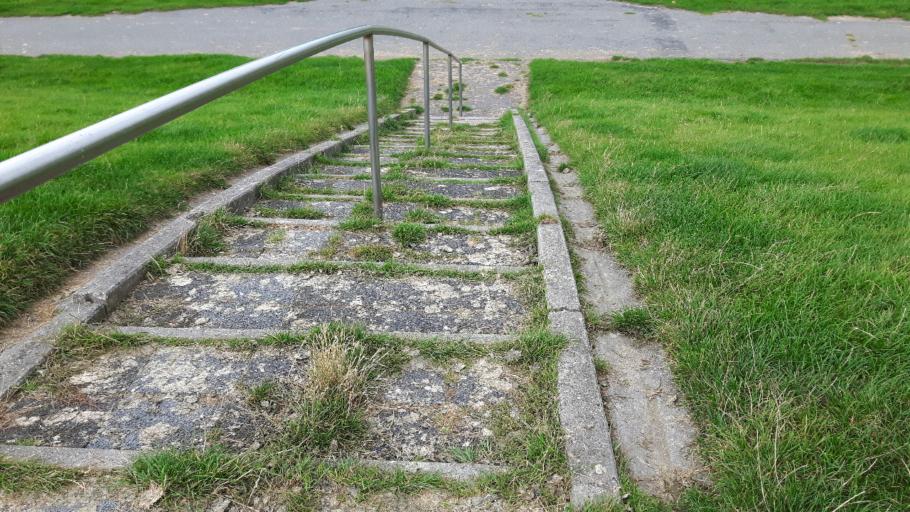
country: NL
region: Friesland
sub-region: Gemeente Ameland
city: Nes
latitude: 53.4425
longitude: 5.8304
